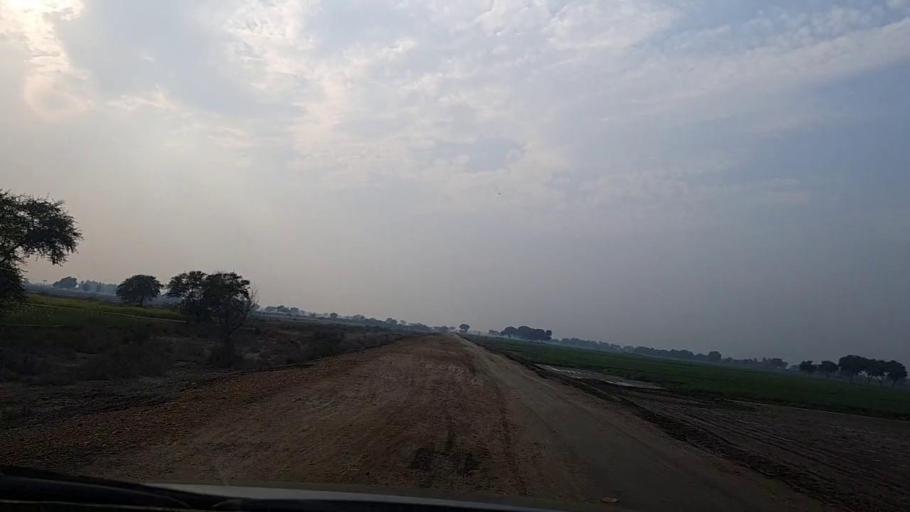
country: PK
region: Sindh
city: Nawabshah
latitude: 26.2737
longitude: 68.3398
